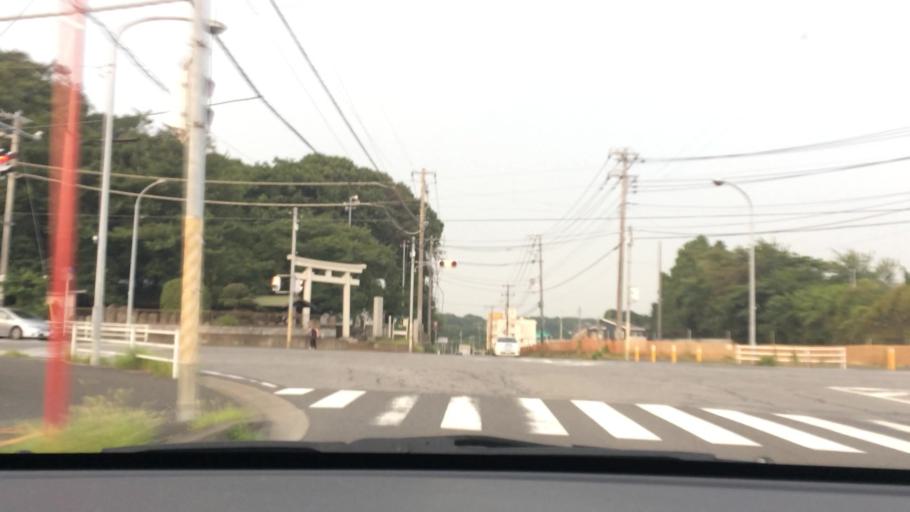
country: JP
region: Chiba
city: Nagareyama
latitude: 35.8692
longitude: 139.9084
